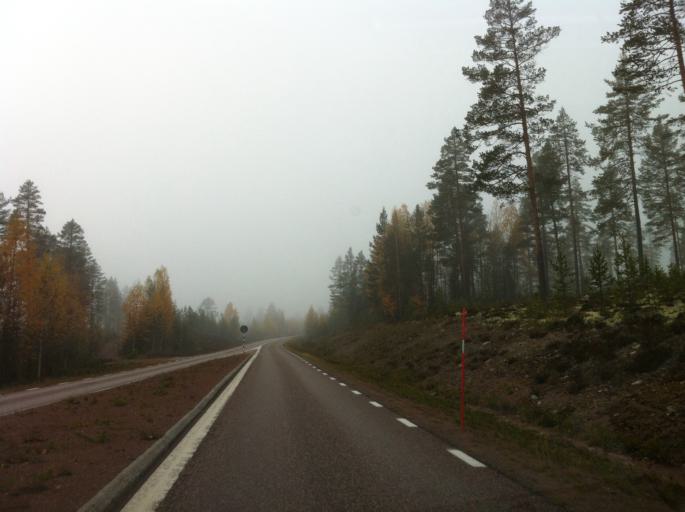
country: NO
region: Hedmark
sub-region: Trysil
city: Innbygda
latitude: 61.6934
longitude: 13.0756
